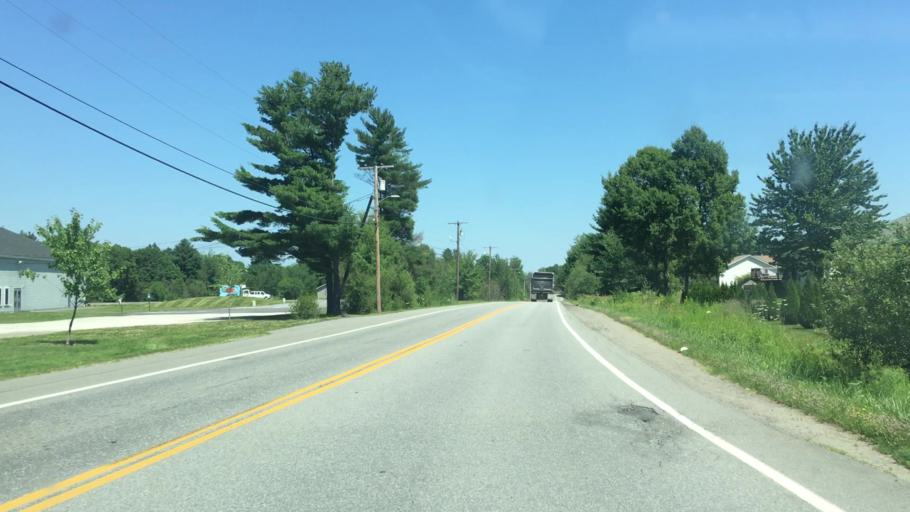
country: US
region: Maine
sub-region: Penobscot County
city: Bangor
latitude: 44.8288
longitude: -68.8140
